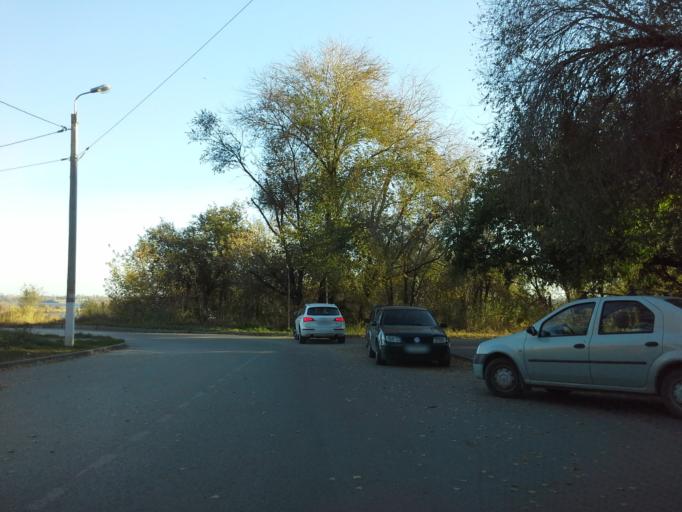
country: RU
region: Volgograd
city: Vodstroy
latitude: 48.8162
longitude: 44.6371
